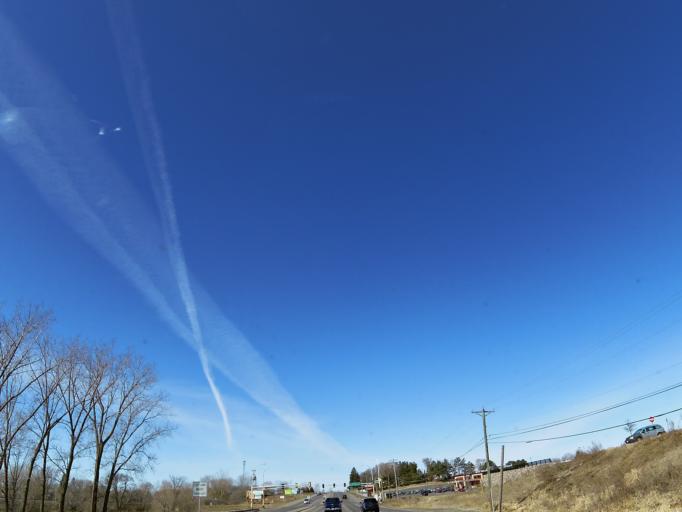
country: US
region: Minnesota
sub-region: Hennepin County
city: Medina
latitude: 45.0440
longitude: -93.5307
